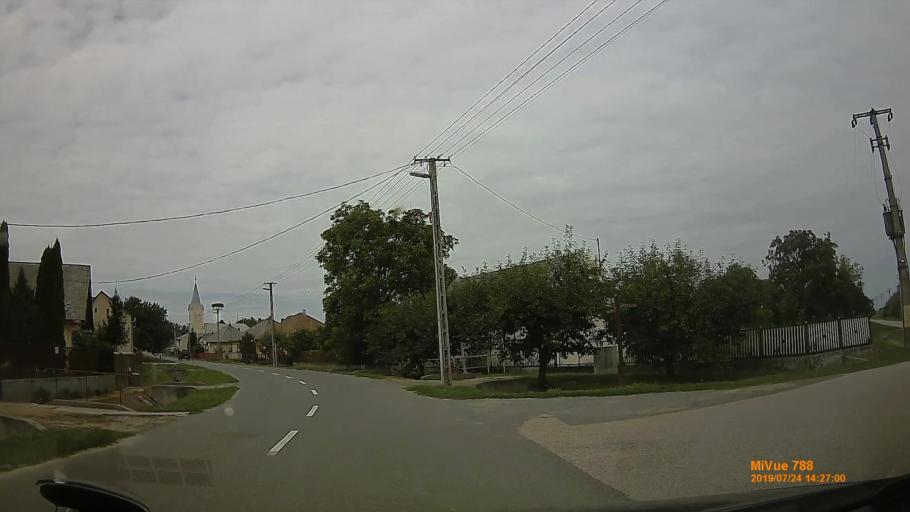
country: HU
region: Szabolcs-Szatmar-Bereg
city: Mandok
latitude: 48.3302
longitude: 22.2654
